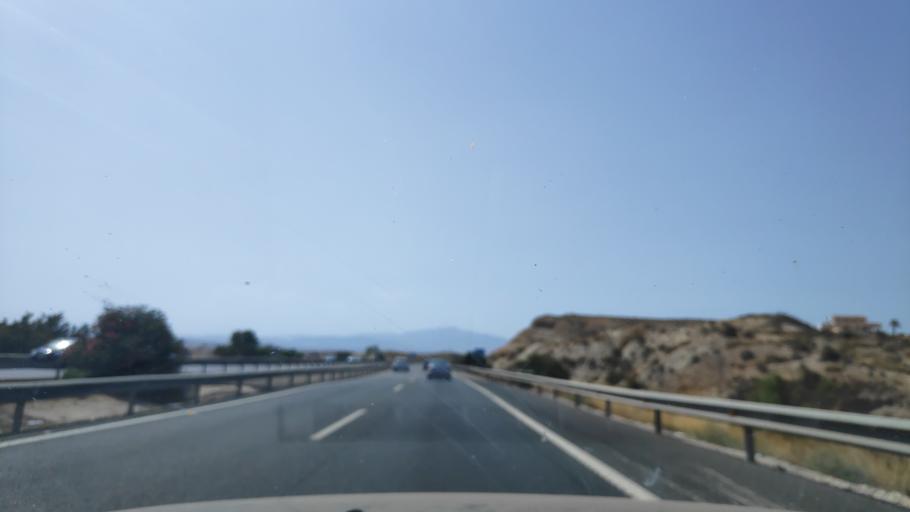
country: ES
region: Murcia
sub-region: Murcia
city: Molina de Segura
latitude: 38.0544
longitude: -1.1810
